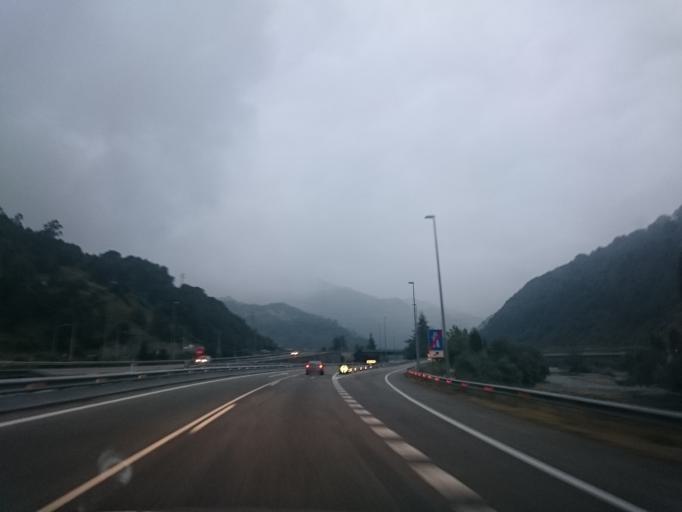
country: ES
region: Asturias
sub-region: Province of Asturias
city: Mieres
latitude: 43.2038
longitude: -5.7873
